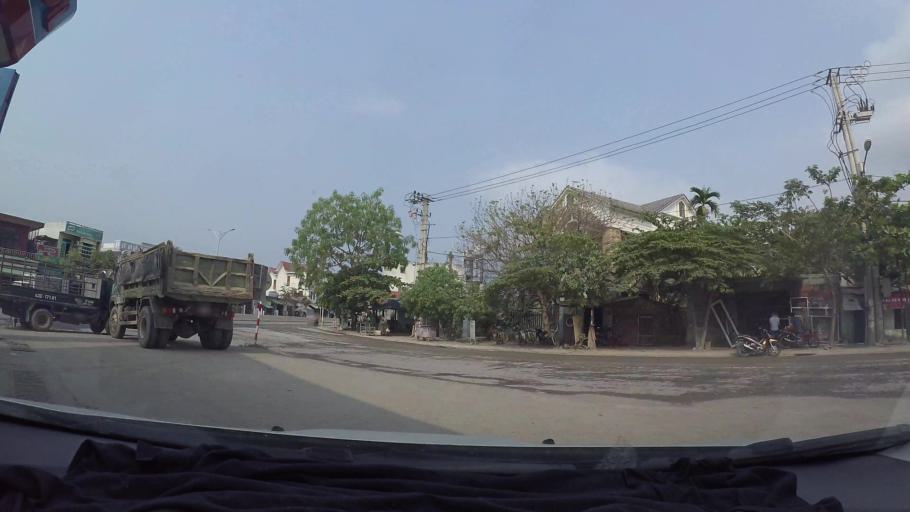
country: VN
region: Da Nang
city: Lien Chieu
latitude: 16.0510
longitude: 108.1511
